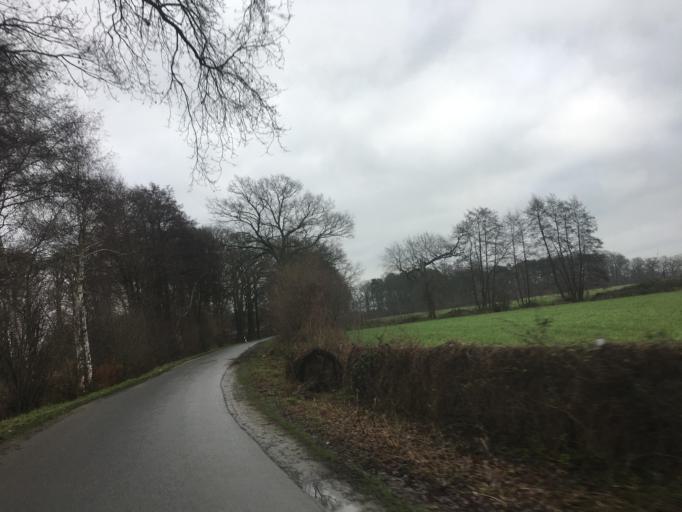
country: DE
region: North Rhine-Westphalia
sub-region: Regierungsbezirk Munster
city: Greven
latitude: 52.0666
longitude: 7.5577
